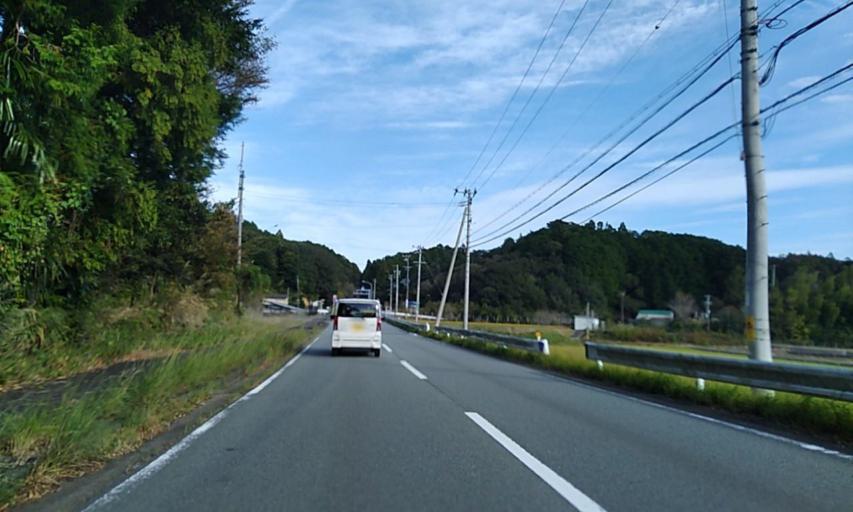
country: JP
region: Mie
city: Ise
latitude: 34.3450
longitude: 136.7187
